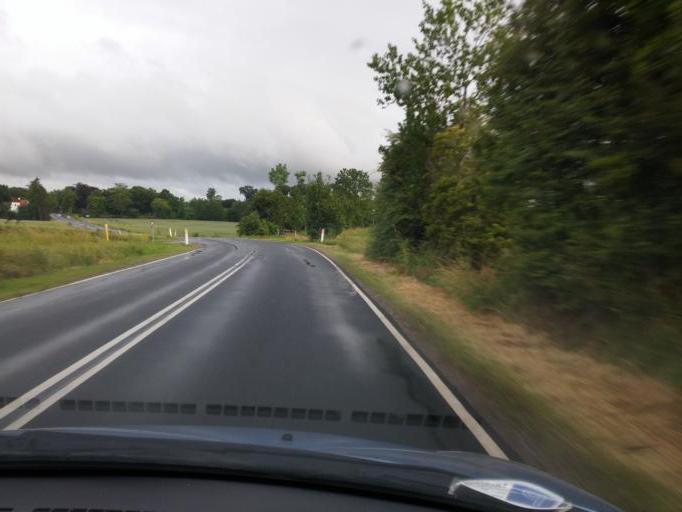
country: DK
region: South Denmark
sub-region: Kerteminde Kommune
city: Kerteminde
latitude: 55.5074
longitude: 10.6506
